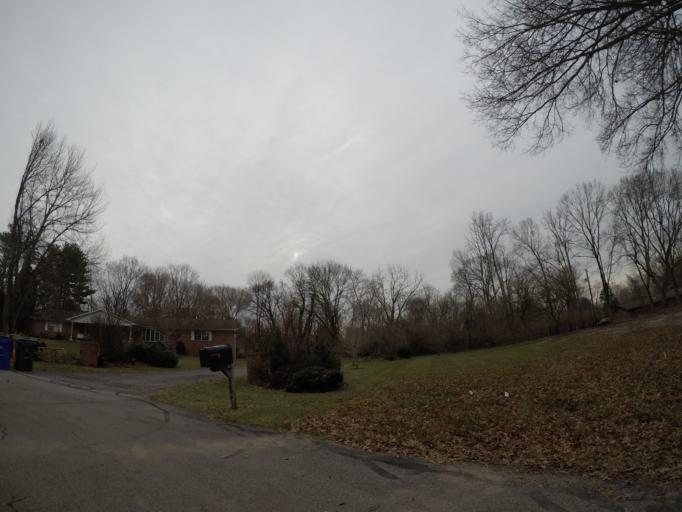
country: US
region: Ohio
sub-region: Franklin County
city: Dublin
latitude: 40.0590
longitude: -83.0968
